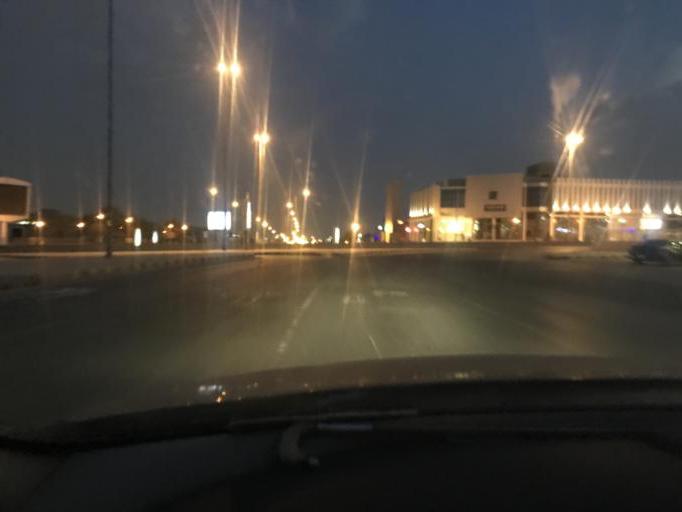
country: SA
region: Ar Riyad
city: Riyadh
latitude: 24.8185
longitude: 46.6874
